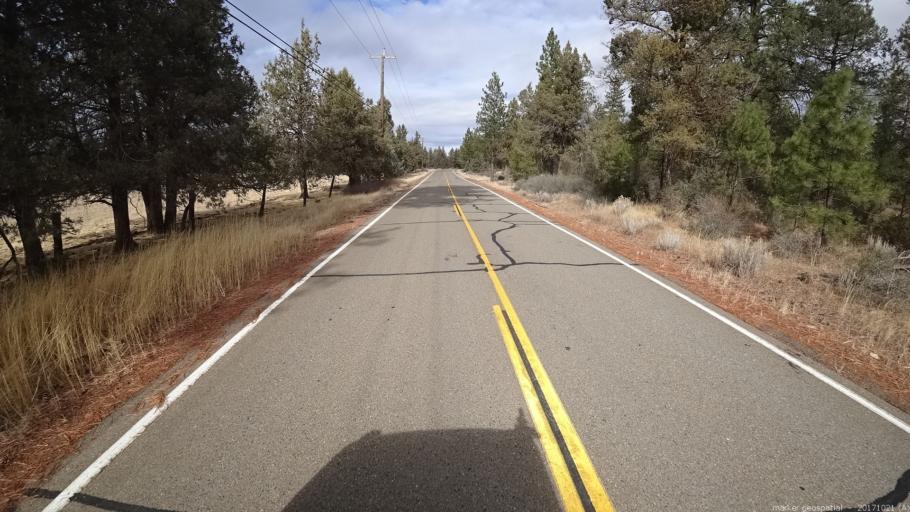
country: US
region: California
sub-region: Shasta County
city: Burney
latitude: 40.9205
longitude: -121.6468
